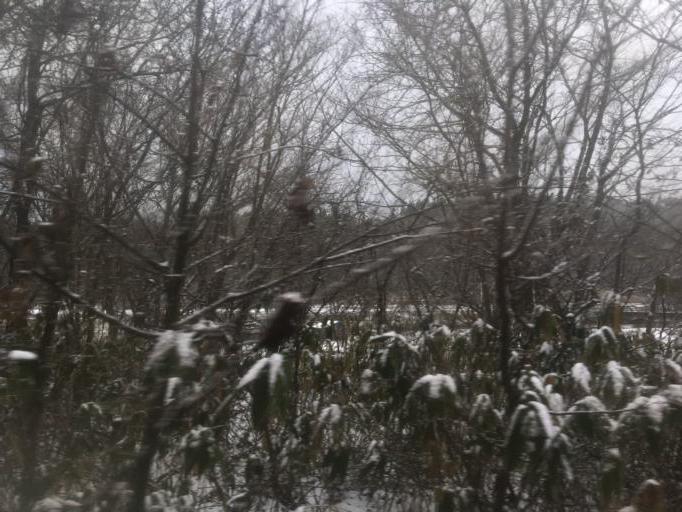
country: JP
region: Aomori
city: Goshogawara
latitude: 41.1343
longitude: 140.5178
